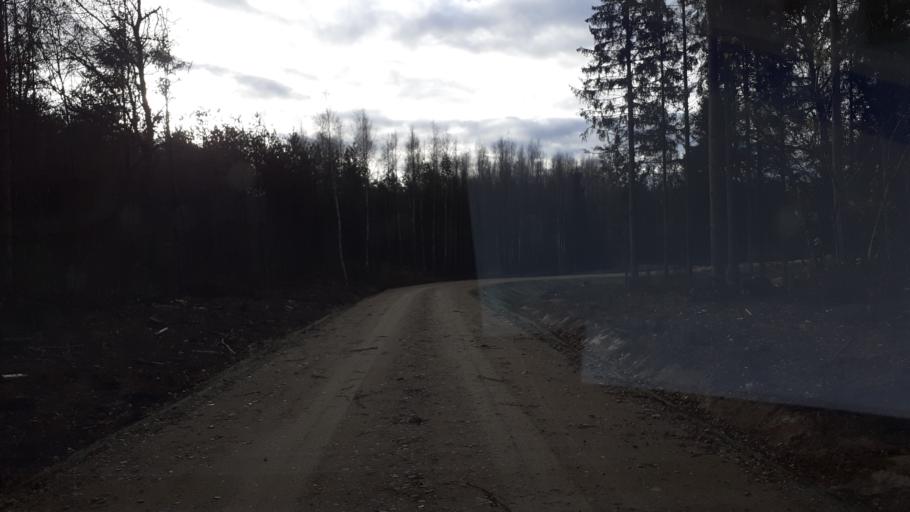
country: LV
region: Skrunda
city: Skrunda
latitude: 56.7879
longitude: 21.8355
